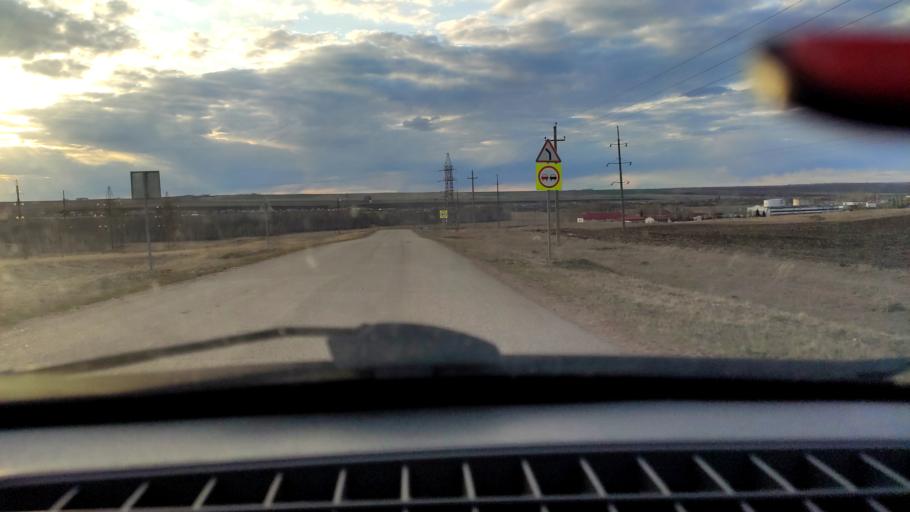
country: RU
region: Bashkortostan
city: Tolbazy
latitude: 54.0157
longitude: 55.7255
